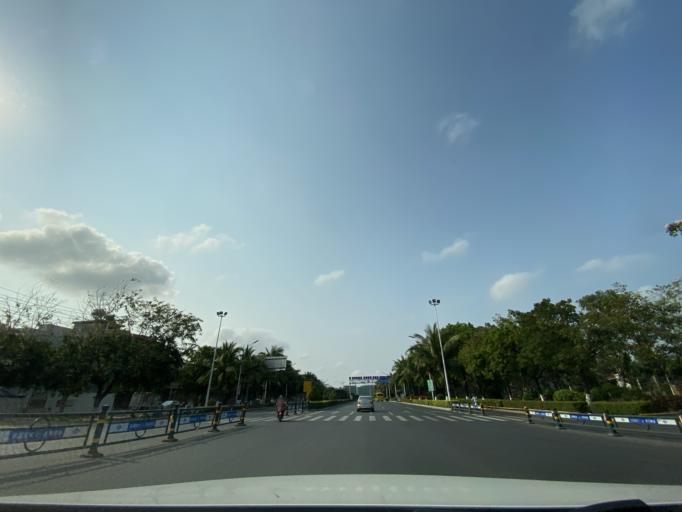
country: CN
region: Hainan
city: Yelin
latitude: 18.5276
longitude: 110.0345
